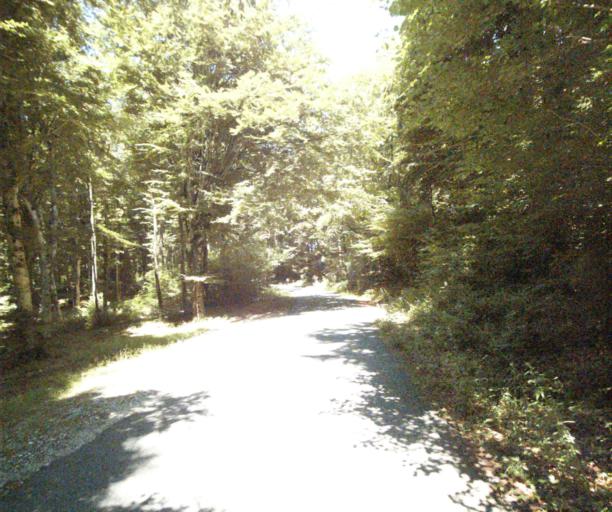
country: FR
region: Midi-Pyrenees
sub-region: Departement du Tarn
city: Dourgne
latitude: 43.4212
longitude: 2.1844
